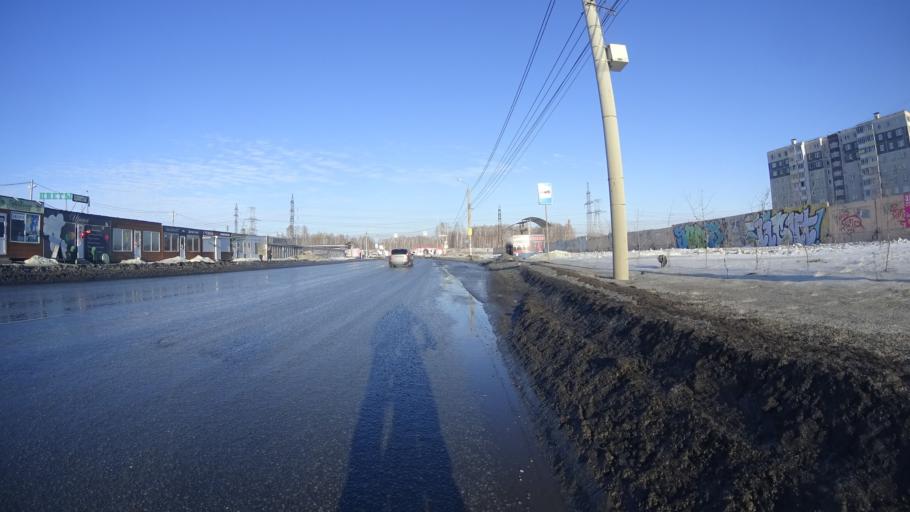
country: RU
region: Chelyabinsk
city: Roshchino
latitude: 55.2194
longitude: 61.2947
